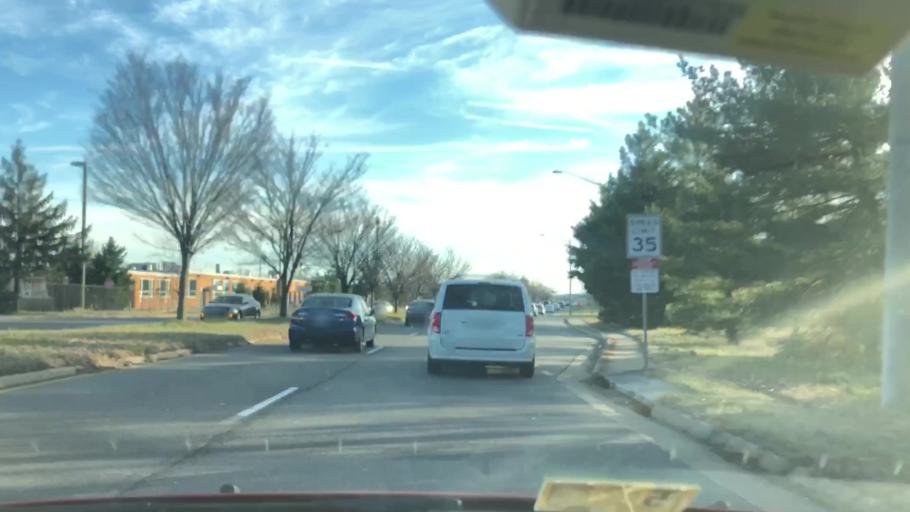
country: US
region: Virginia
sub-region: Fairfax County
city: Franconia
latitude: 38.7829
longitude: -77.1358
